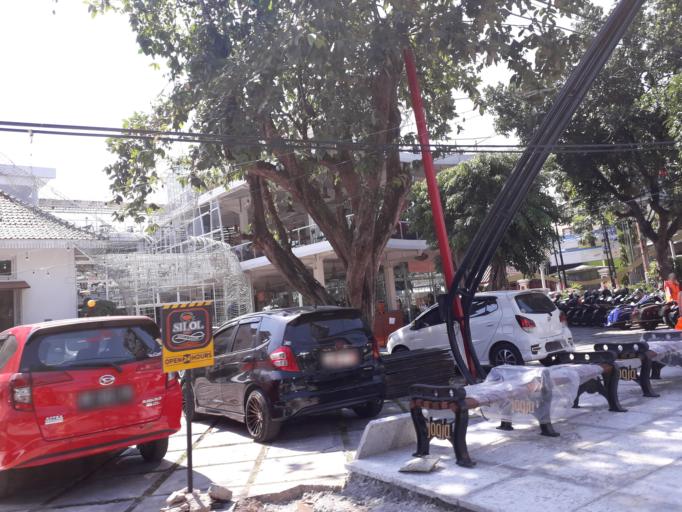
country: ID
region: Daerah Istimewa Yogyakarta
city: Yogyakarta
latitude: -7.7846
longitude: 110.3747
